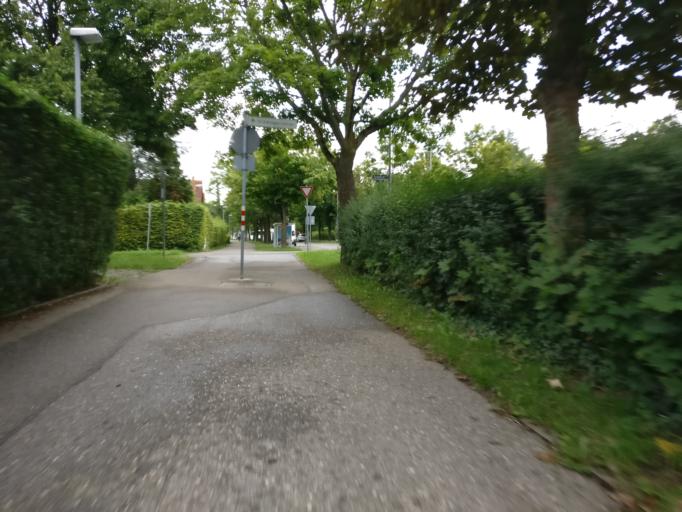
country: DE
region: Baden-Wuerttemberg
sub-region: Karlsruhe Region
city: Weingarten
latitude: 49.0079
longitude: 8.4904
